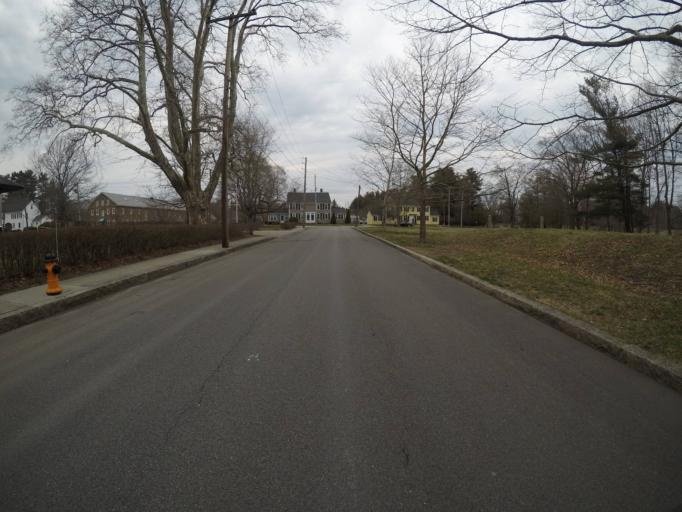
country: US
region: Massachusetts
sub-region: Bristol County
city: Easton
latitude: 42.0693
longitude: -71.1030
